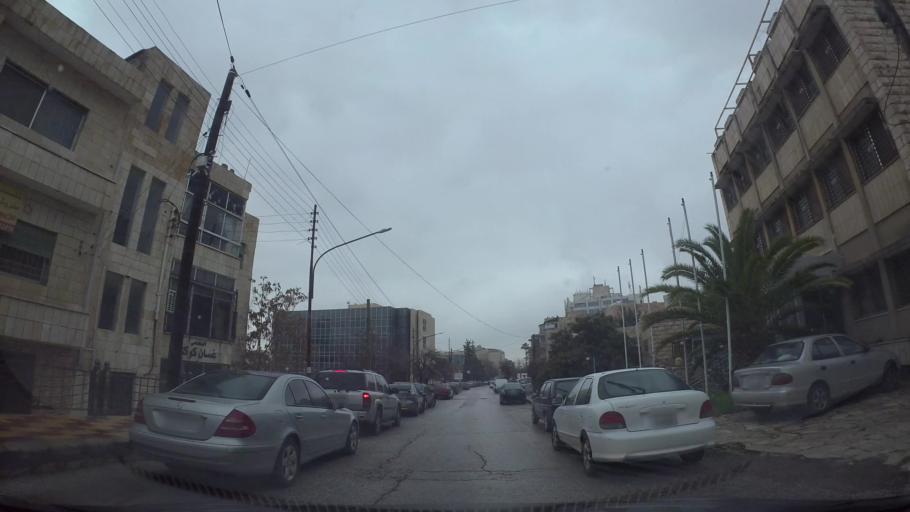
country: JO
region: Amman
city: Amman
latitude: 31.9561
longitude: 35.9109
